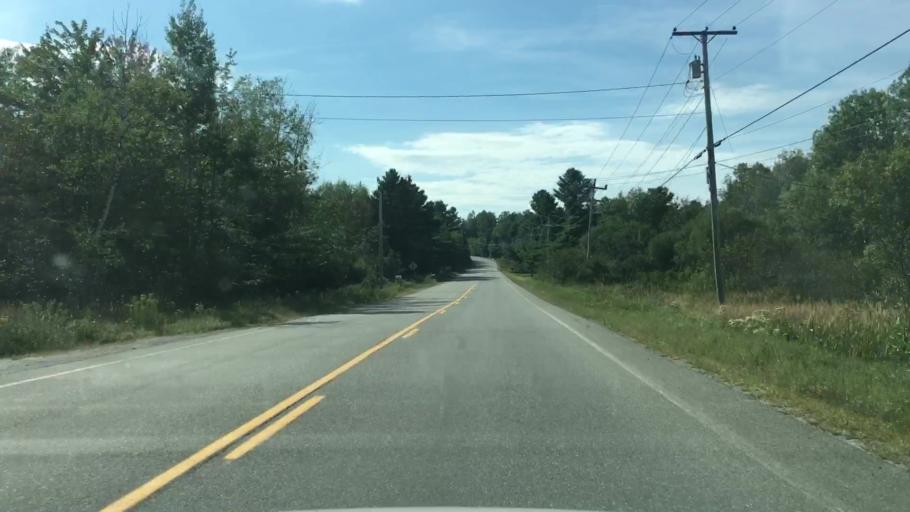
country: US
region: Maine
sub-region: Penobscot County
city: Lincoln
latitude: 45.3931
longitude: -68.5213
